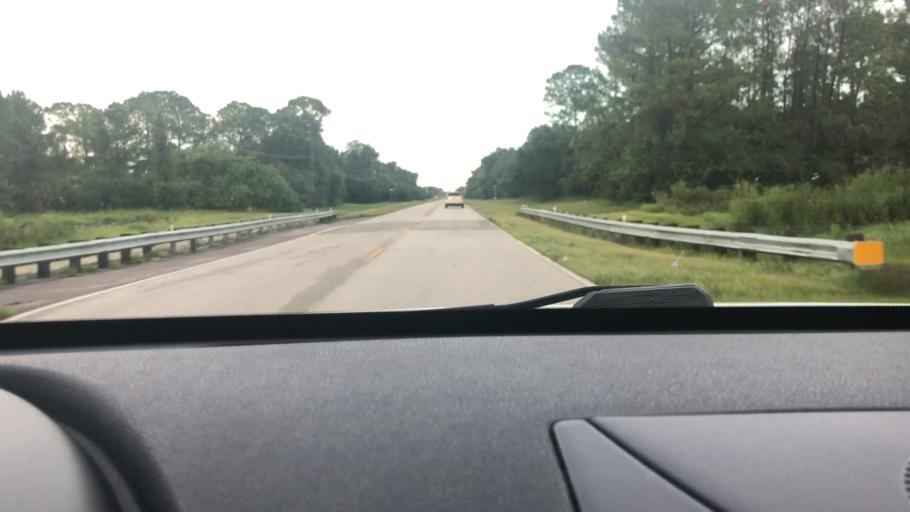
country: US
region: Florida
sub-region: Charlotte County
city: Port Charlotte
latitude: 27.0690
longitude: -82.1269
